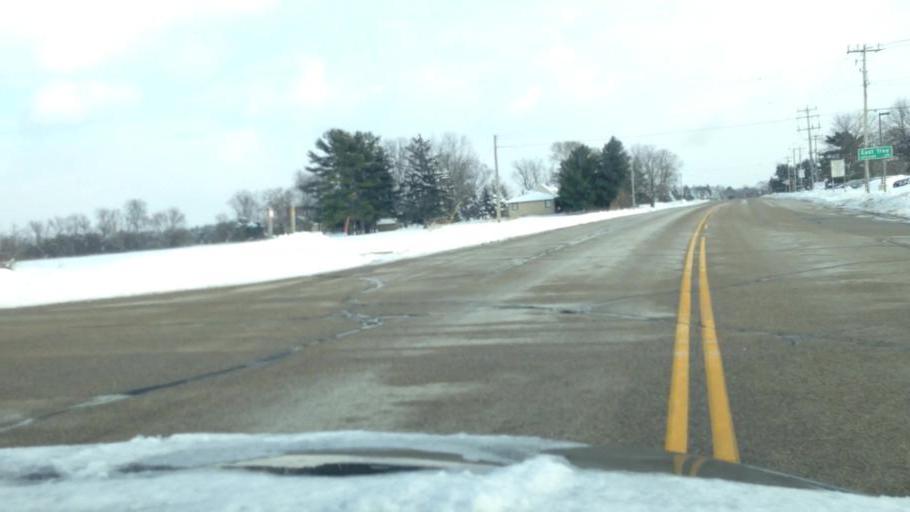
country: US
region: Wisconsin
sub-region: Walworth County
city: East Troy
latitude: 42.7923
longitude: -88.4253
